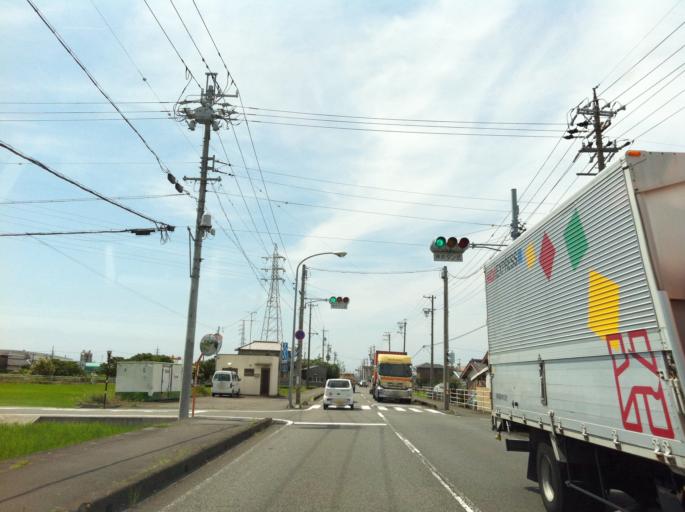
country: JP
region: Shizuoka
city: Shimada
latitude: 34.7887
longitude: 138.2536
